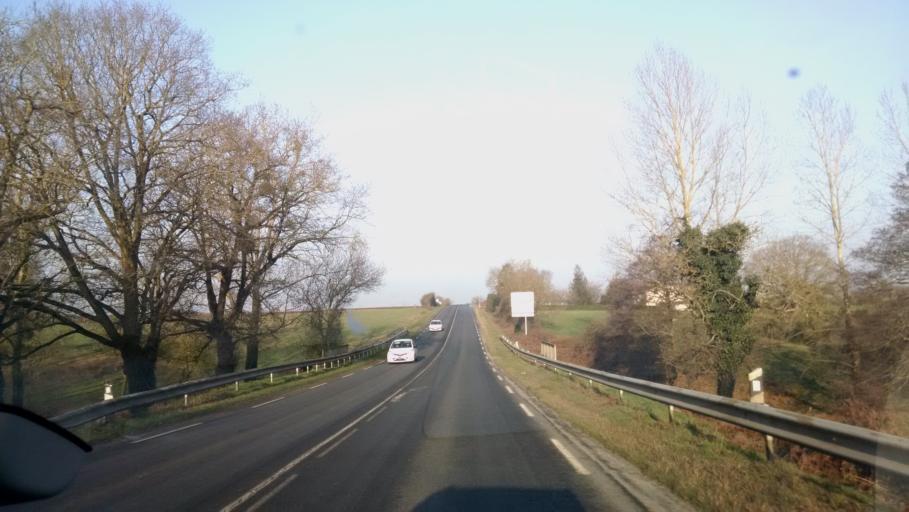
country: FR
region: Pays de la Loire
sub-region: Departement de la Loire-Atlantique
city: Remouille
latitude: 47.0600
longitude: -1.3785
